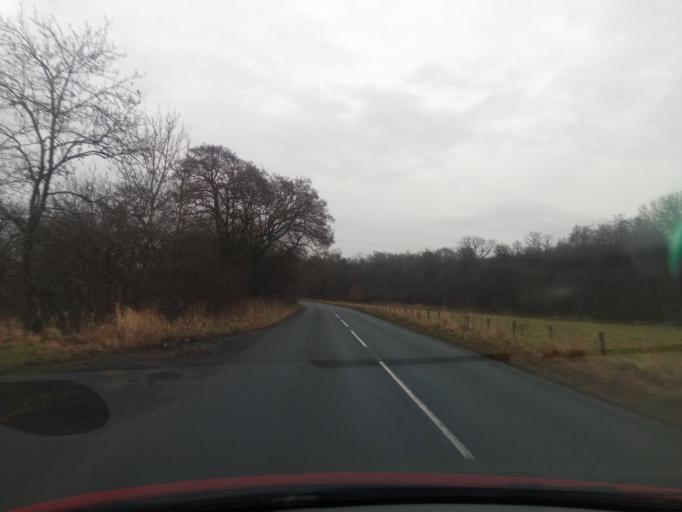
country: GB
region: England
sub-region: Northumberland
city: Rochester
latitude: 55.1653
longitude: -2.4136
